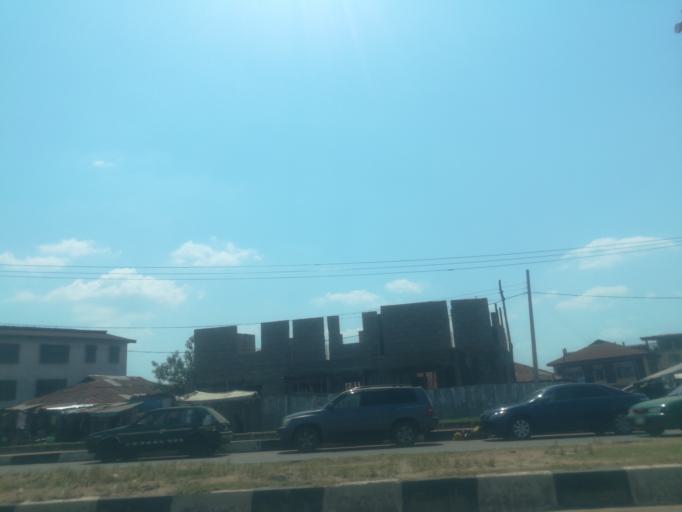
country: NG
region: Ogun
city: Abeokuta
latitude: 7.1531
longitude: 3.3493
